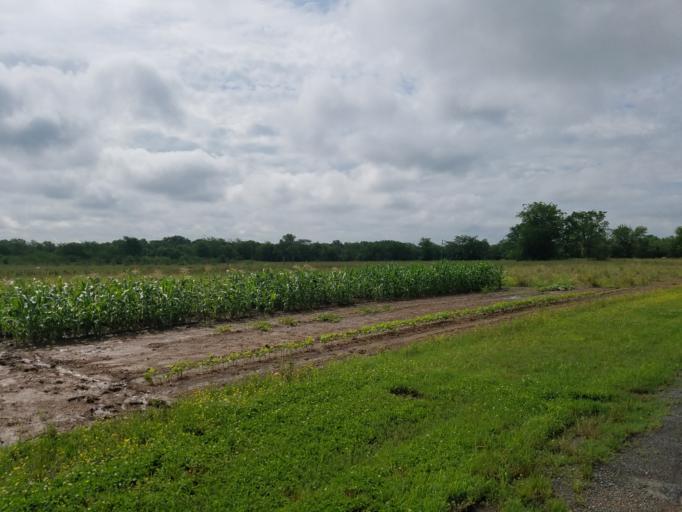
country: US
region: Oklahoma
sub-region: Coal County
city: Coalgate
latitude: 34.4343
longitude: -96.4135
